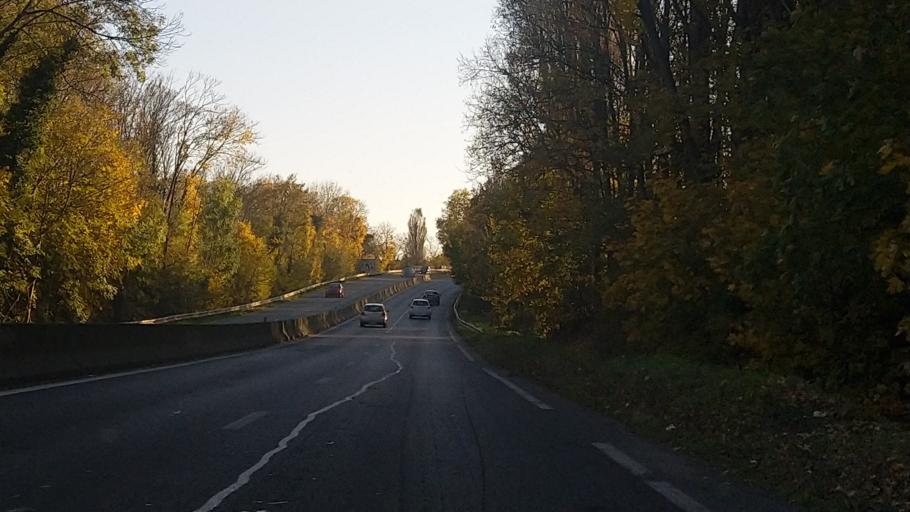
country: FR
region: Ile-de-France
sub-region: Departement du Val-d'Oise
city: Saint-Brice-sous-Foret
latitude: 48.9991
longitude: 2.3602
